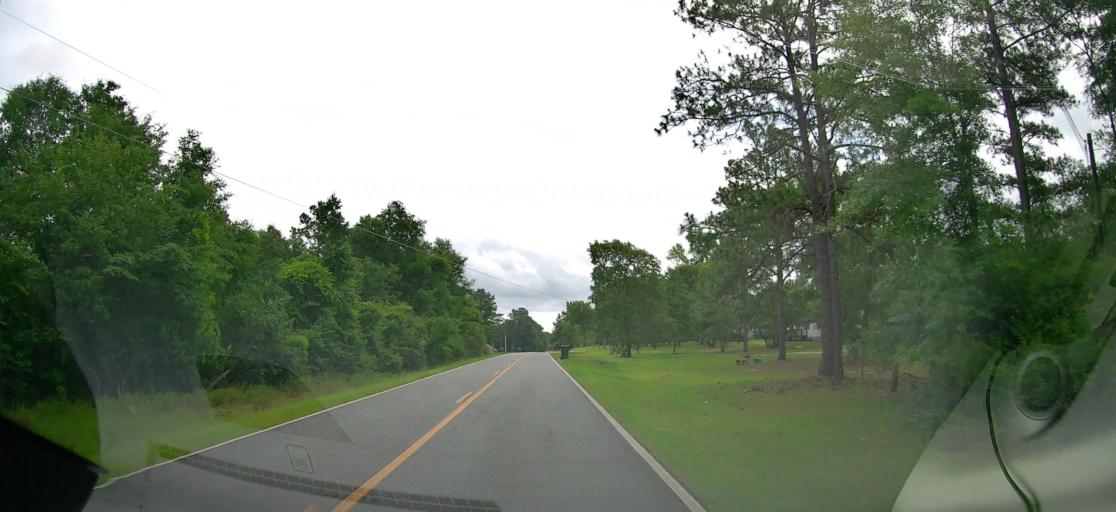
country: US
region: Georgia
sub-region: Bibb County
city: West Point
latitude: 32.7923
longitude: -83.7903
